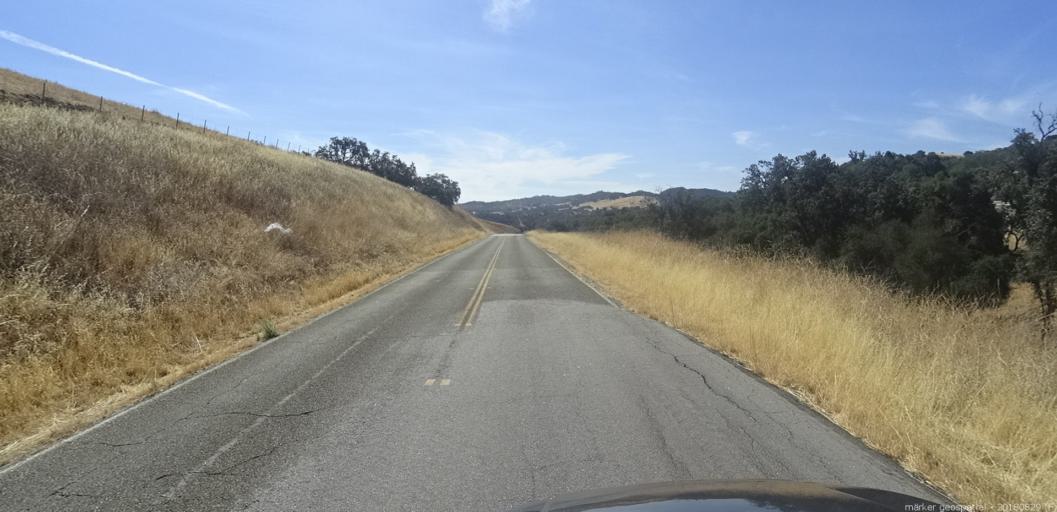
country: US
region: California
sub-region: San Luis Obispo County
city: Lake Nacimiento
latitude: 35.8462
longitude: -121.0485
